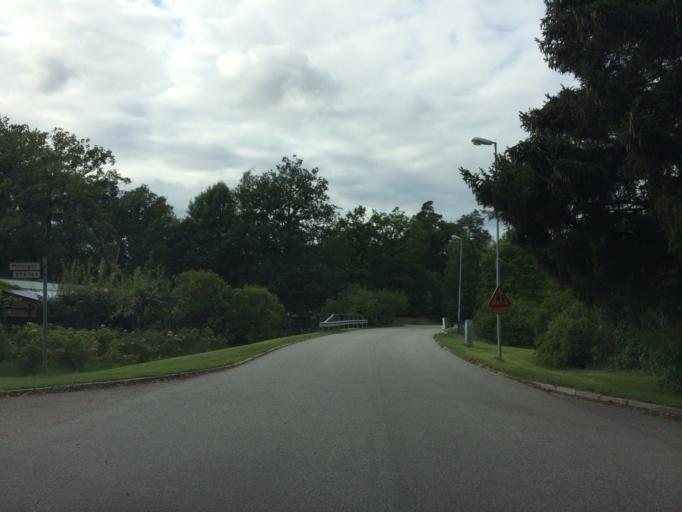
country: SE
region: Stockholm
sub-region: Sollentuna Kommun
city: Sollentuna
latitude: 59.4620
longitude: 17.9056
